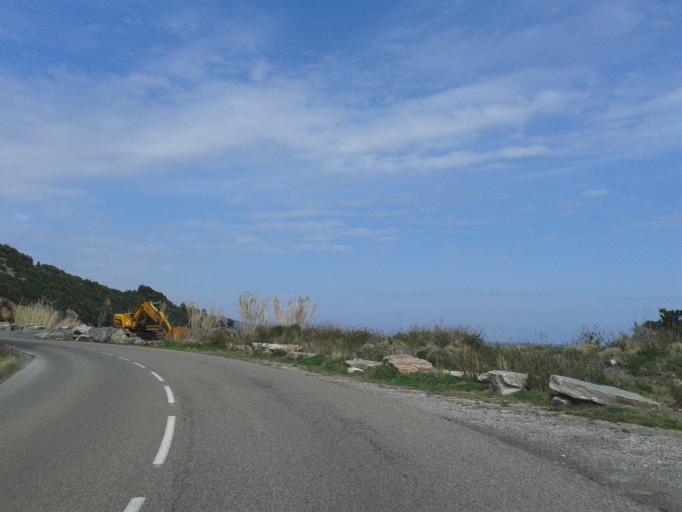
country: FR
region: Corsica
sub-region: Departement de la Haute-Corse
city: Brando
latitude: 42.8643
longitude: 9.4818
